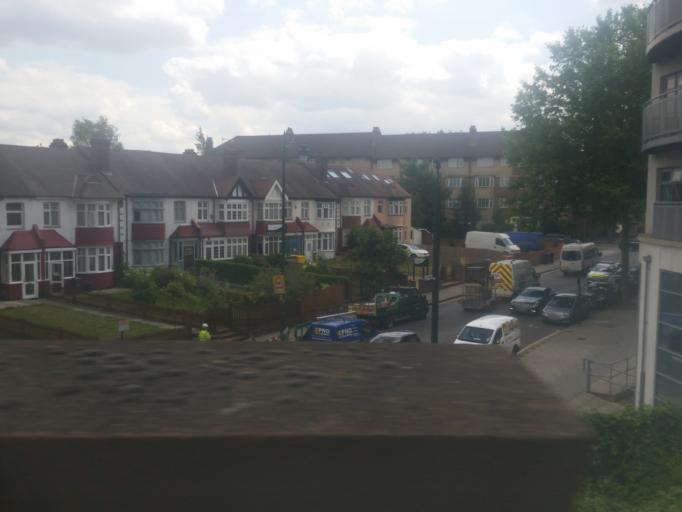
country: GB
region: England
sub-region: Greater London
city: Brixton Hill
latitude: 51.4387
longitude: -0.1061
